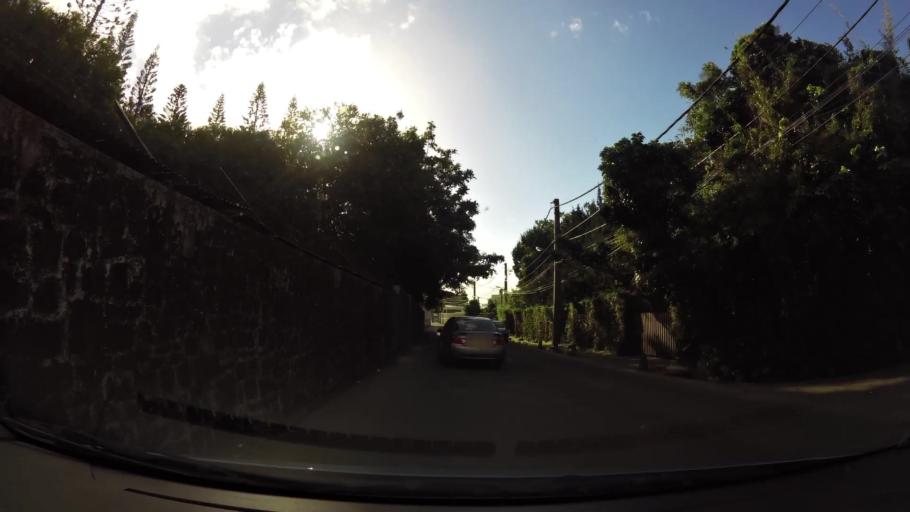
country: MU
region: Plaines Wilhems
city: Vacoas
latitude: -20.3095
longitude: 57.4954
